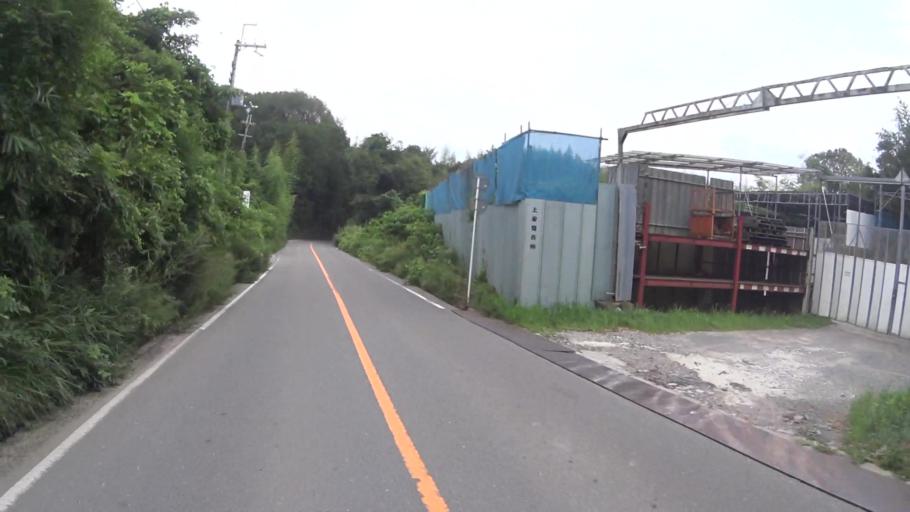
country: JP
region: Kyoto
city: Tanabe
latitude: 34.7905
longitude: 135.7471
